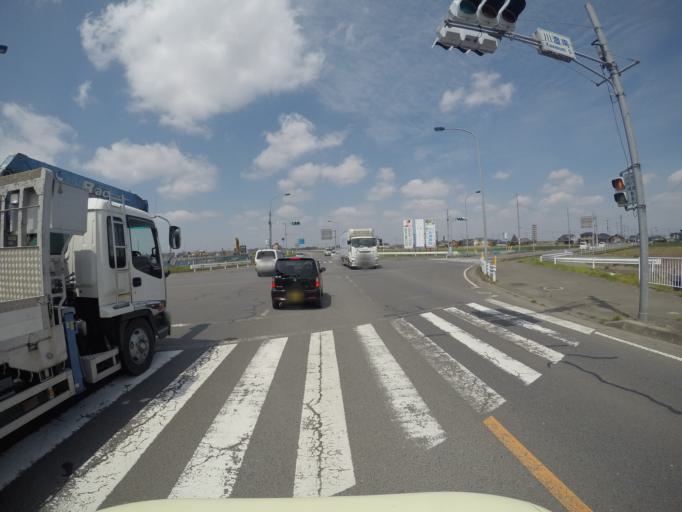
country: JP
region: Ibaraki
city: Shimodate
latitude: 36.3236
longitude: 139.9959
